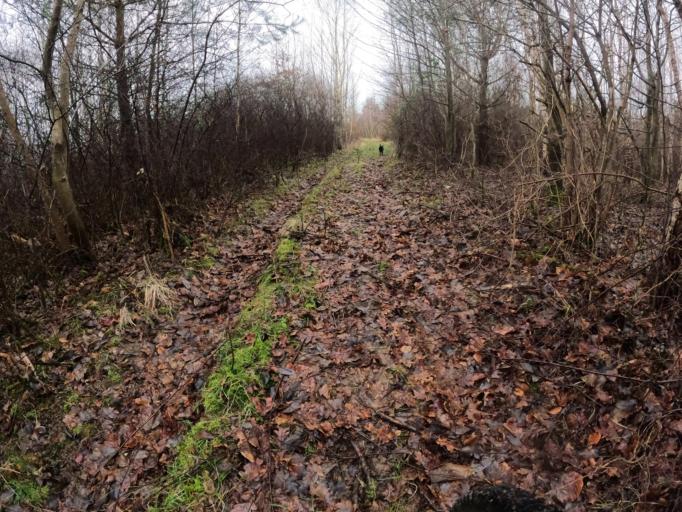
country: PL
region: West Pomeranian Voivodeship
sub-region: Powiat slawienski
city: Darlowo
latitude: 54.3945
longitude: 16.5181
